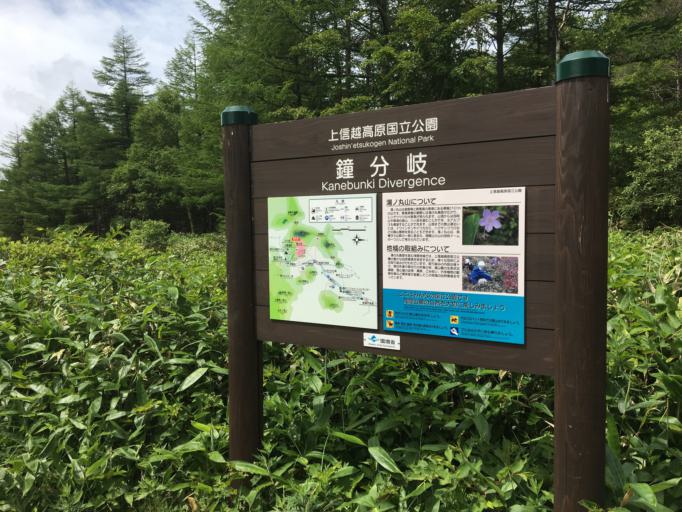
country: JP
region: Nagano
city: Komoro
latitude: 36.4326
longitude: 138.4091
